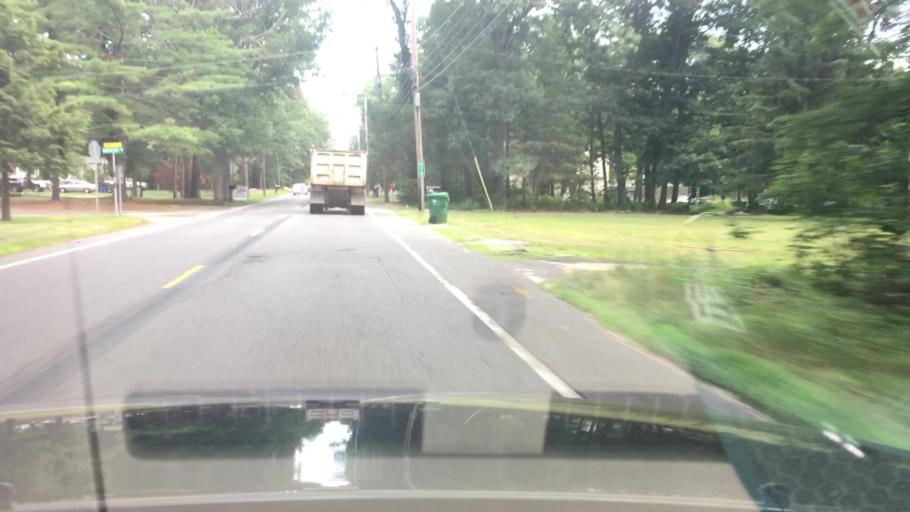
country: US
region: New Jersey
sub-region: Ocean County
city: Vista Center
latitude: 40.1177
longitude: -74.3920
